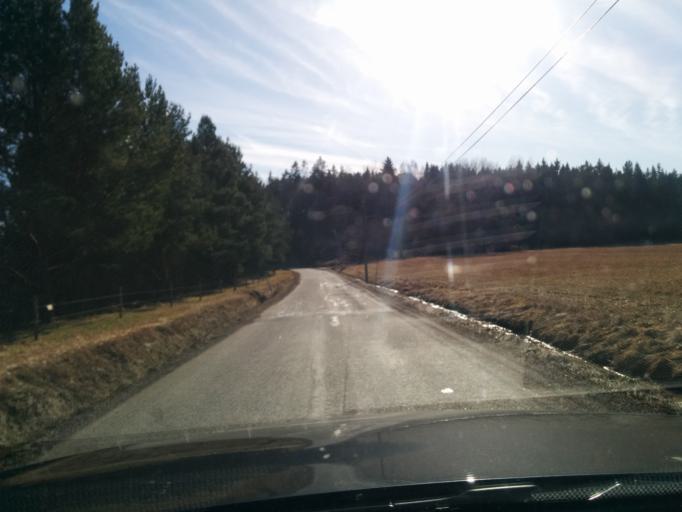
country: SE
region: Stockholm
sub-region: Vallentuna Kommun
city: Vallentuna
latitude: 59.5075
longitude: 18.0089
